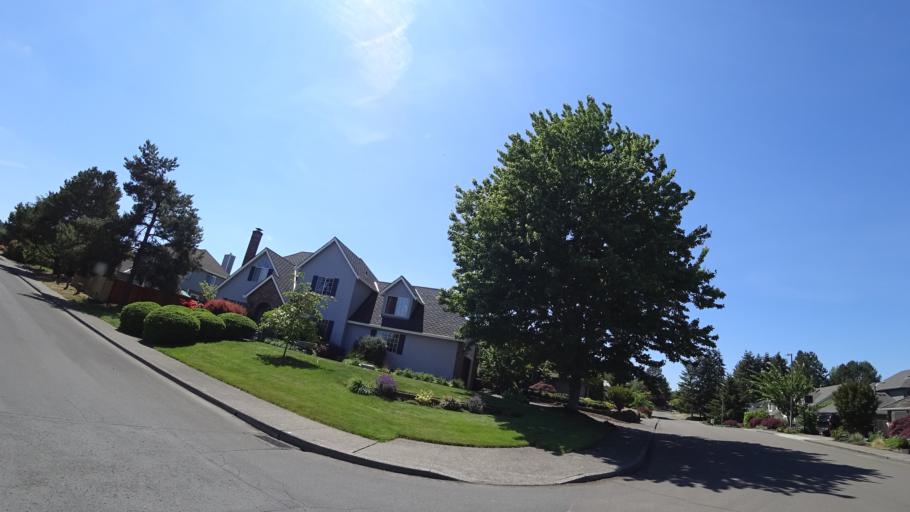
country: US
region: Oregon
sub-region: Washington County
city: King City
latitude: 45.4329
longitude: -122.8111
